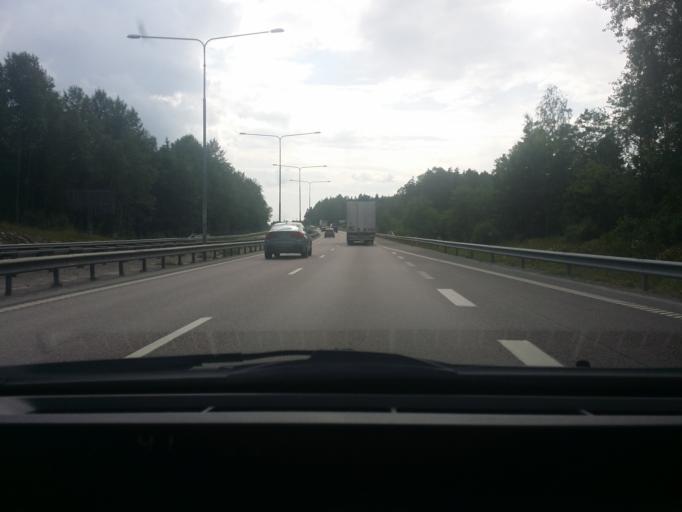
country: SE
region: Vaestmanland
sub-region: Vasteras
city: Vasteras
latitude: 59.6045
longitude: 16.4485
